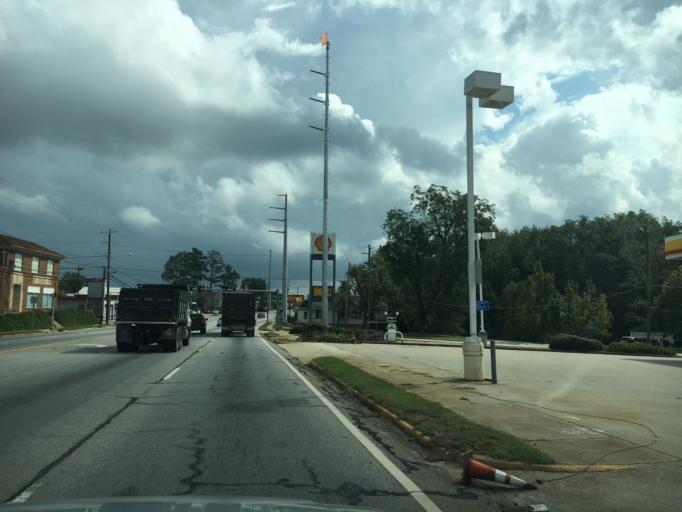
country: US
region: Georgia
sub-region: Elbert County
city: Elberton
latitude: 34.1075
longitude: -82.8573
